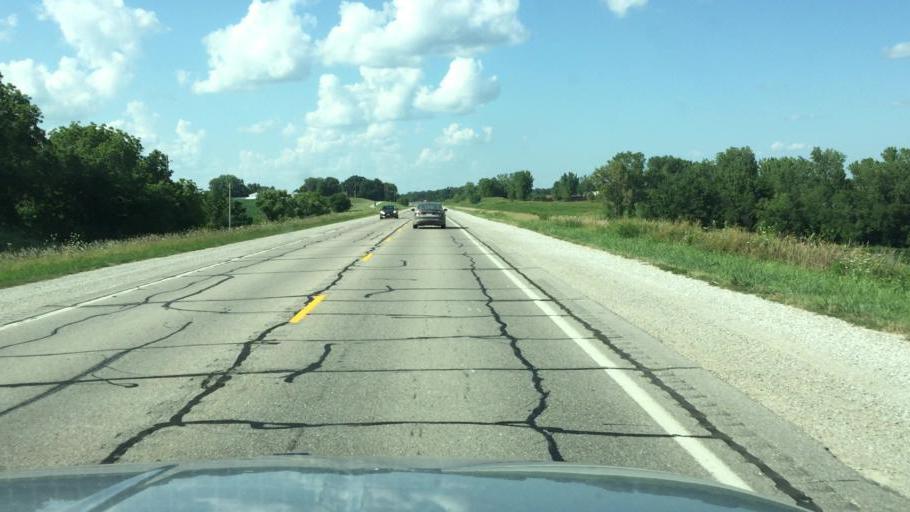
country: US
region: Iowa
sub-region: Jasper County
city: Newton
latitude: 41.6628
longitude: -93.0767
